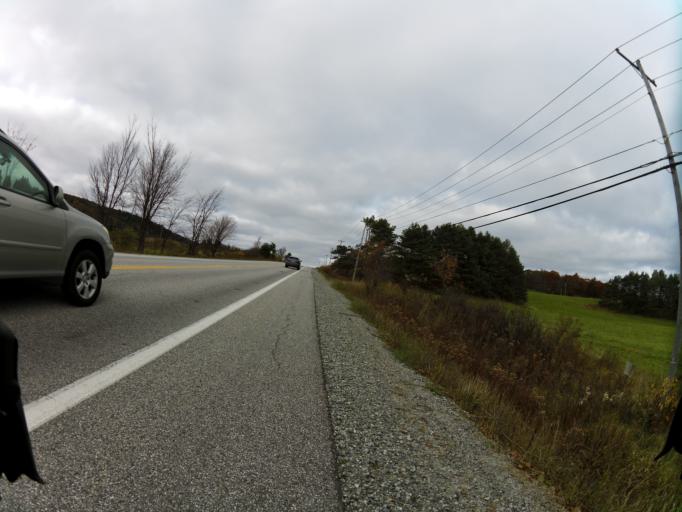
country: CA
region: Quebec
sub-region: Outaouais
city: Wakefield
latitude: 45.6039
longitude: -75.9049
